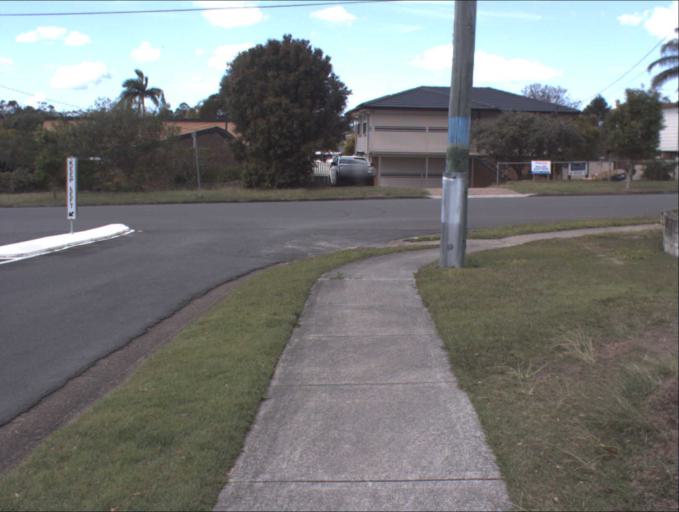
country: AU
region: Queensland
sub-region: Logan
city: Logan Reserve
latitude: -27.6811
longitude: 153.0855
